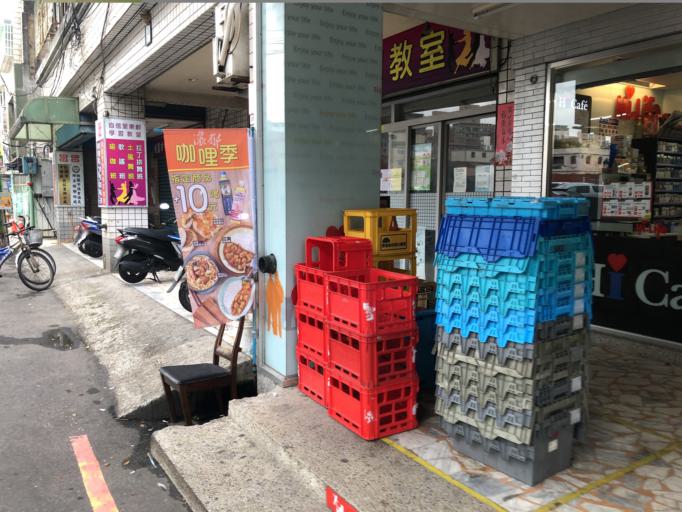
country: TW
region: Taiwan
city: Taoyuan City
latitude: 24.9653
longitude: 121.2521
